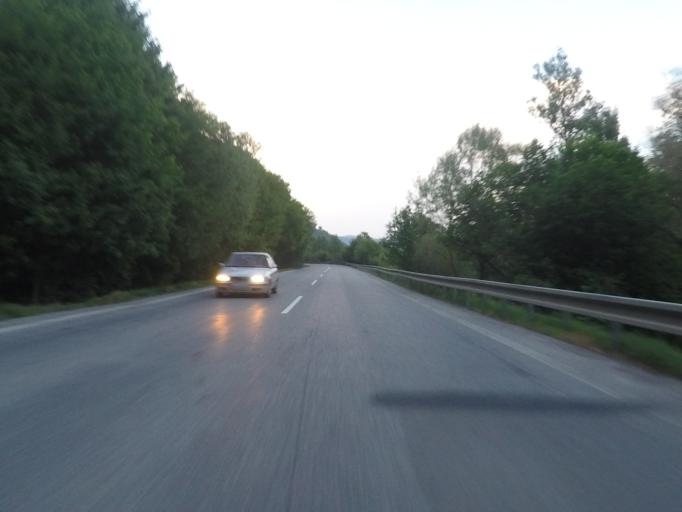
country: SK
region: Banskobystricky
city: Rimavska Sobota
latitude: 48.5174
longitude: 19.9436
